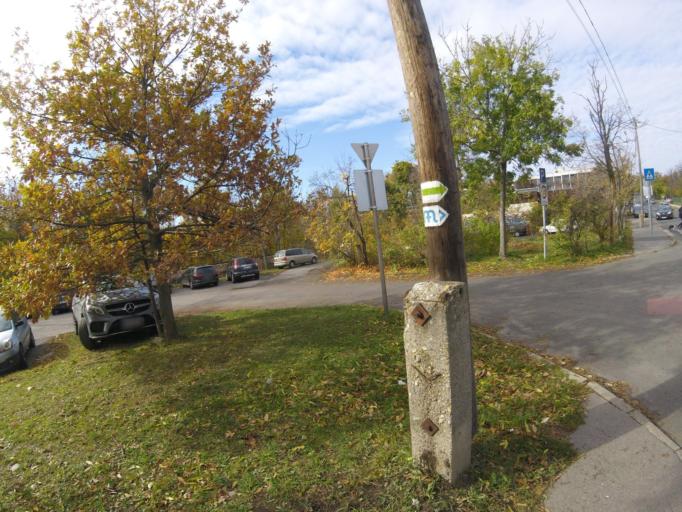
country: HU
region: Pest
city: Budaors
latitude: 47.5004
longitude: 18.9706
